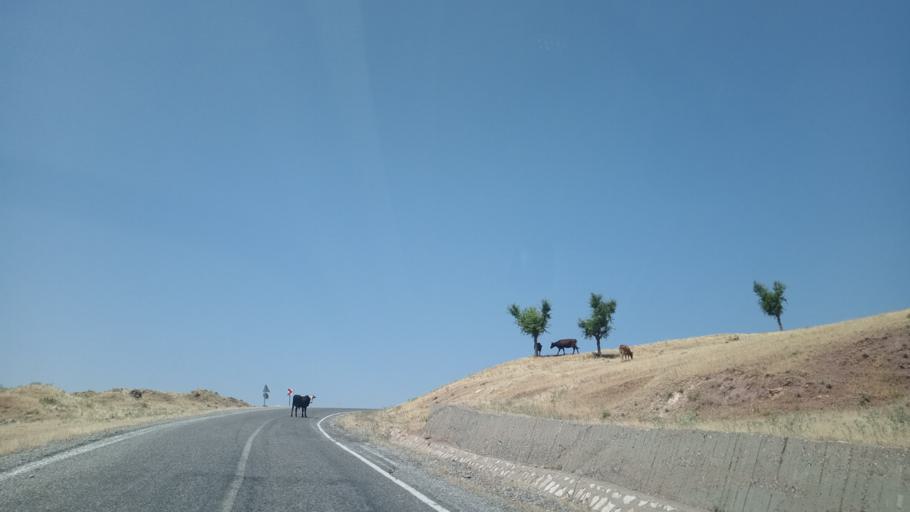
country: TR
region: Siirt
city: Dilektepe
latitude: 38.0657
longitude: 41.8322
